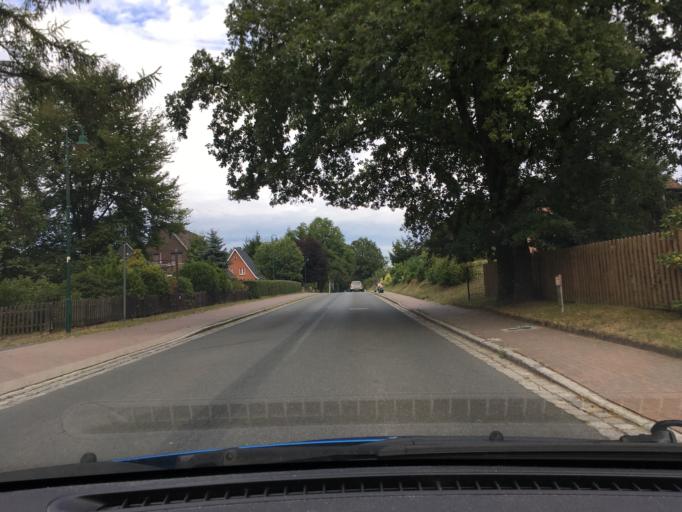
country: DE
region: Lower Saxony
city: Undeloh
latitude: 53.1988
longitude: 9.9823
